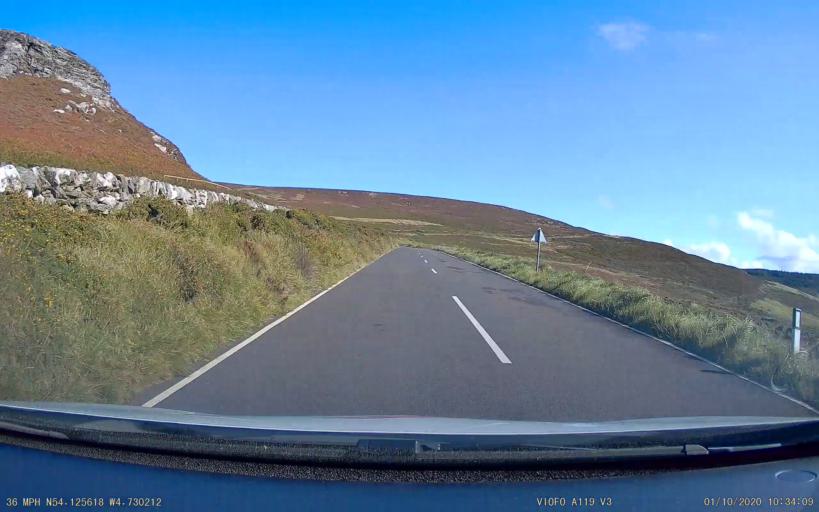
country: IM
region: Port Erin
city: Port Erin
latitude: 54.1259
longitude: -4.7290
